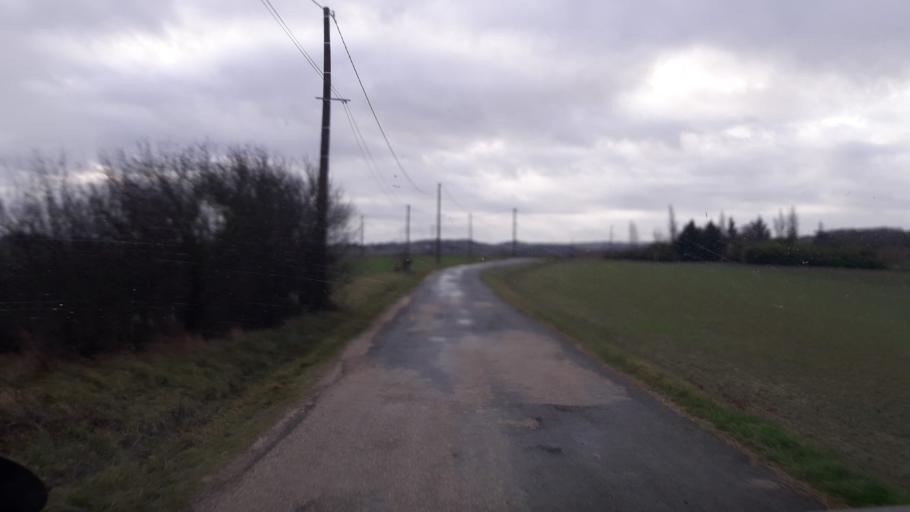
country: FR
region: Midi-Pyrenees
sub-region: Departement de la Haute-Garonne
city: Marquefave
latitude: 43.3087
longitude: 1.2435
